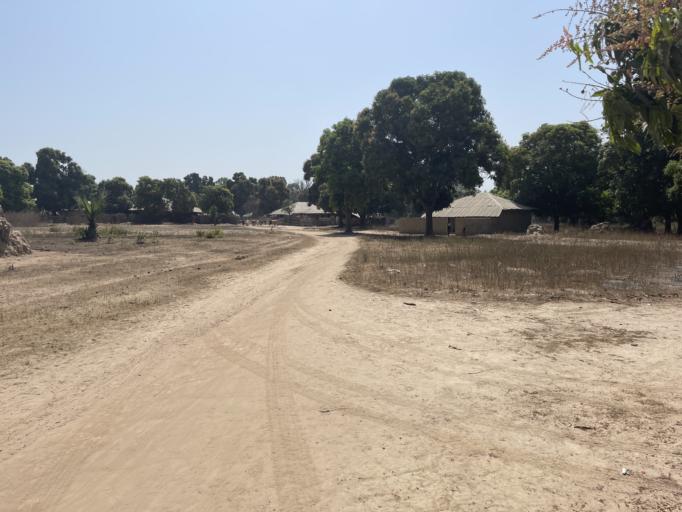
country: SN
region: Sedhiou
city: Sedhiou
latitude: 12.4636
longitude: -15.5954
